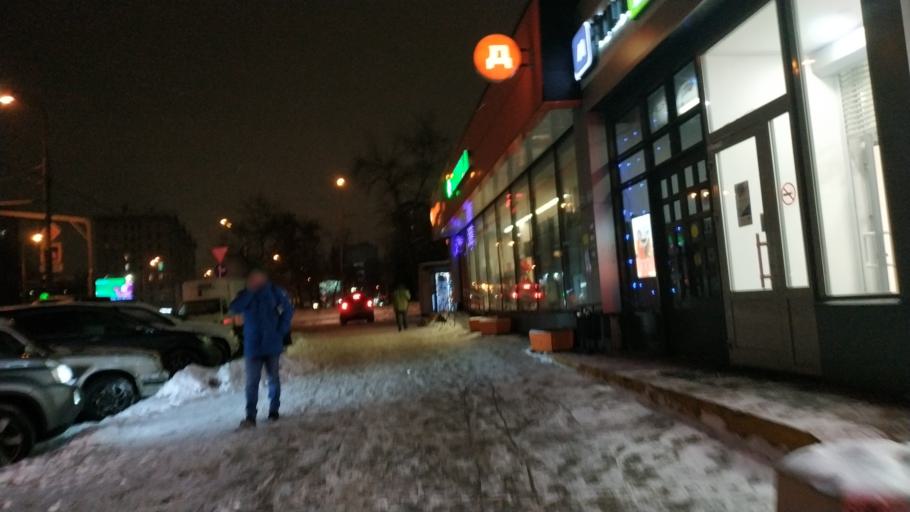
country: RU
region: Moscow
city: Taganskiy
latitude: 55.7298
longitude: 37.6747
